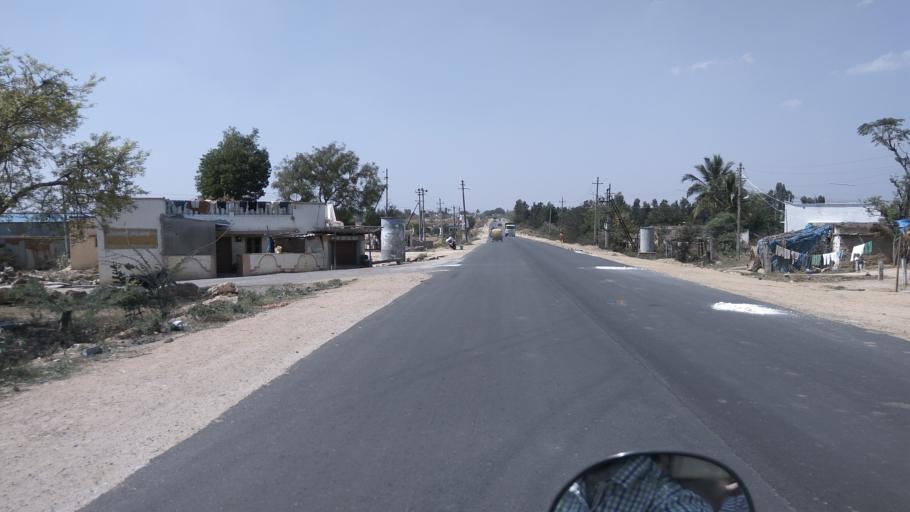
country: IN
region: Karnataka
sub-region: Kolar
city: Mulbagal
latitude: 13.1780
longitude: 78.3531
